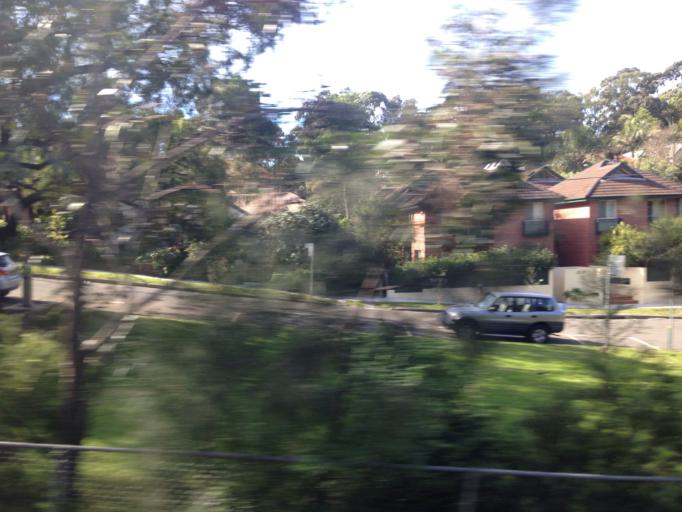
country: AU
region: New South Wales
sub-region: North Sydney
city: St Leonards
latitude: -33.8269
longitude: 151.1956
